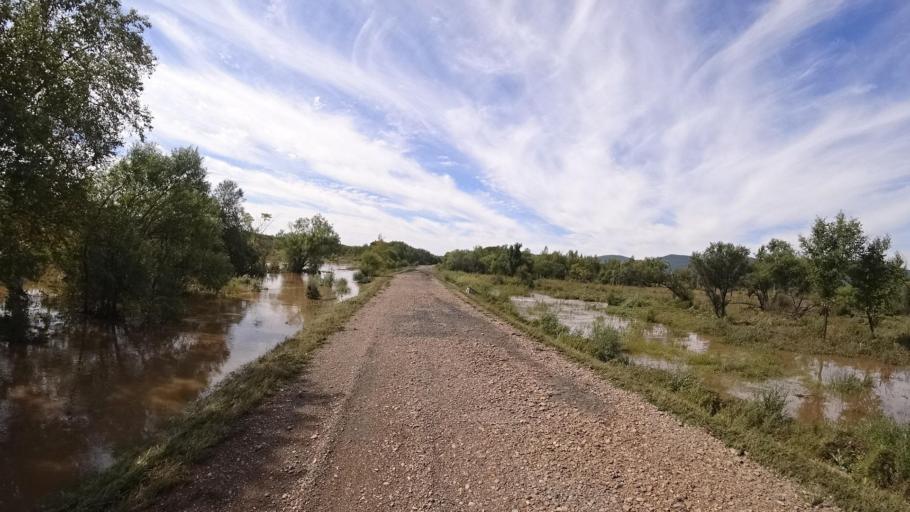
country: RU
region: Primorskiy
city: Kirovskiy
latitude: 44.7677
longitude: 133.6202
